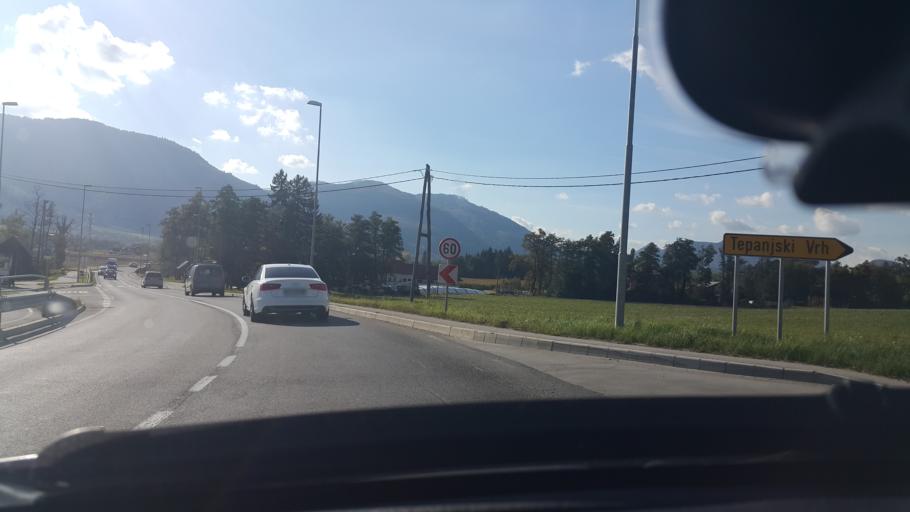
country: SI
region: Slovenska Konjice
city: Slovenske Konjice
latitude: 46.3431
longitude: 15.4539
